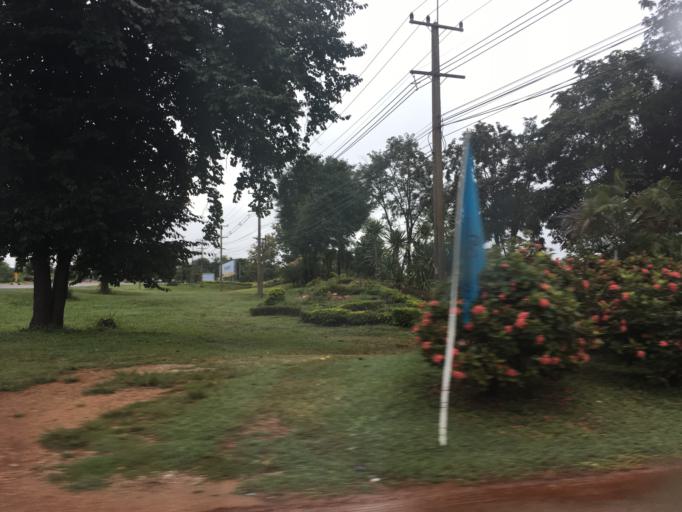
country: TH
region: Kanchanaburi
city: Sai Yok
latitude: 14.1312
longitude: 99.1612
